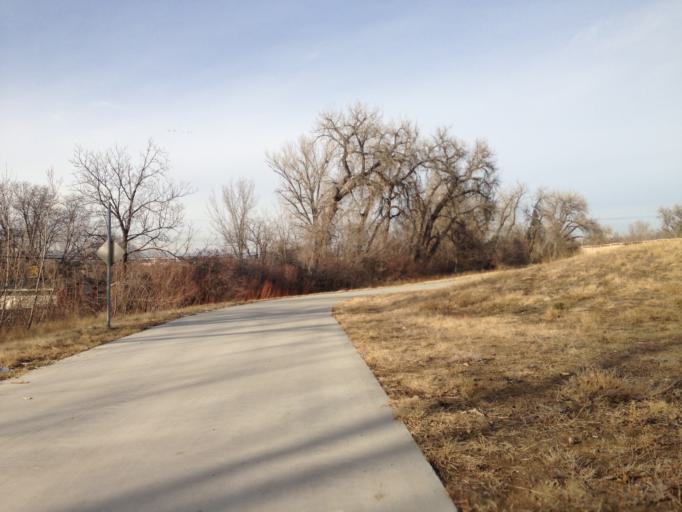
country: US
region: Colorado
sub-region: Adams County
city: Westminster
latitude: 39.8433
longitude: -105.0428
